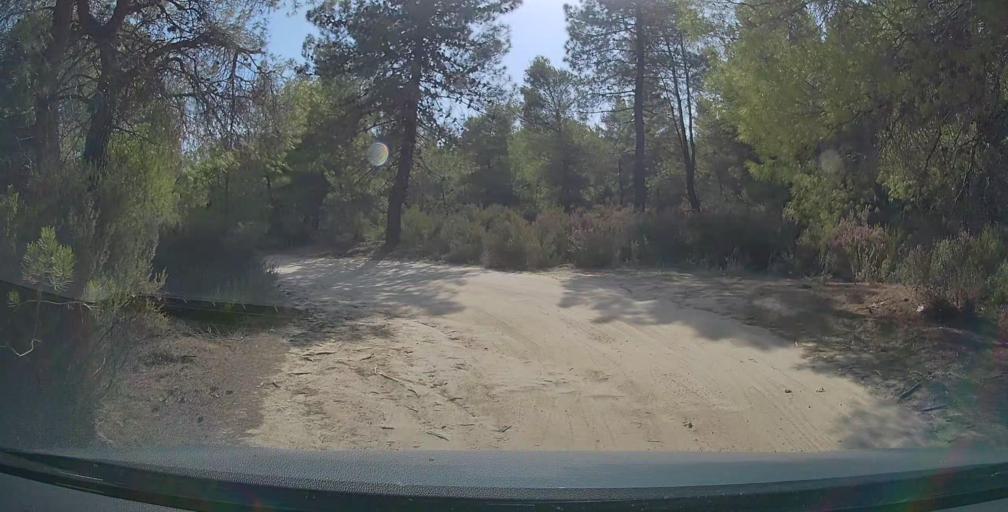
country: GR
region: Central Macedonia
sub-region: Nomos Chalkidikis
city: Sarti
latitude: 40.1268
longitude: 23.9511
